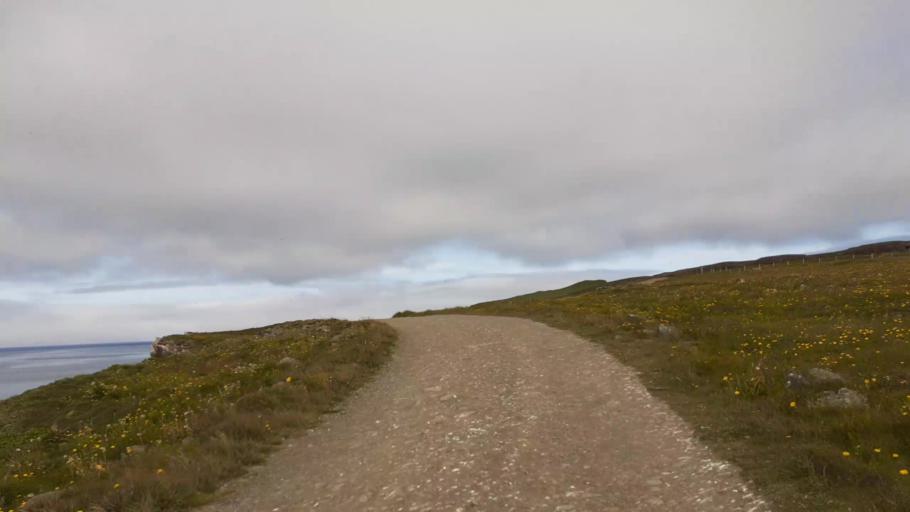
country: IS
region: Northeast
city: Dalvik
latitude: 66.5502
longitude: -18.0254
